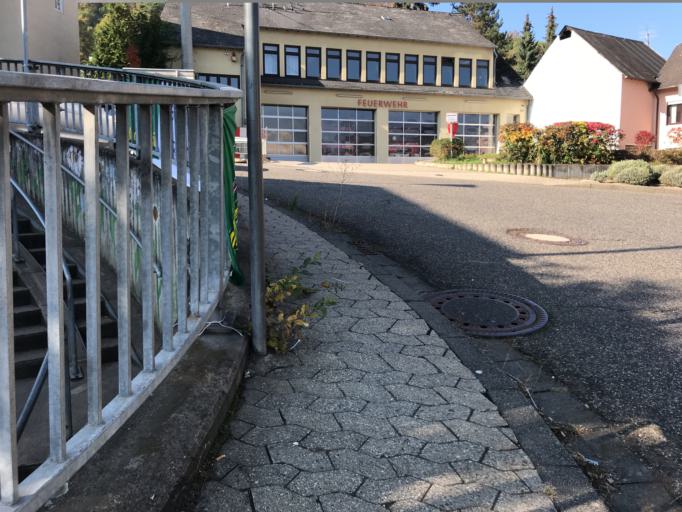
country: DE
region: Rheinland-Pfalz
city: Kobern-Gondorf
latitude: 50.3083
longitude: 7.4578
